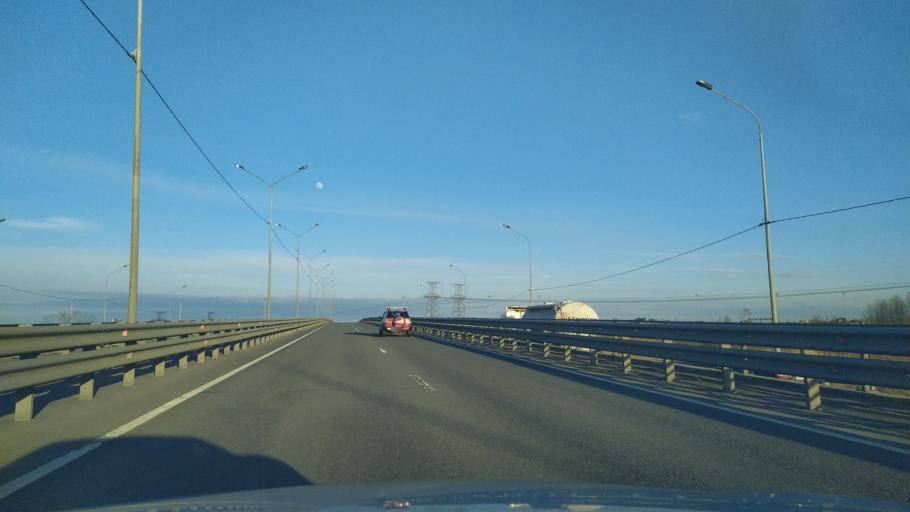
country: RU
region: St.-Petersburg
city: Aleksandrovskaya
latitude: 59.7460
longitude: 30.3050
